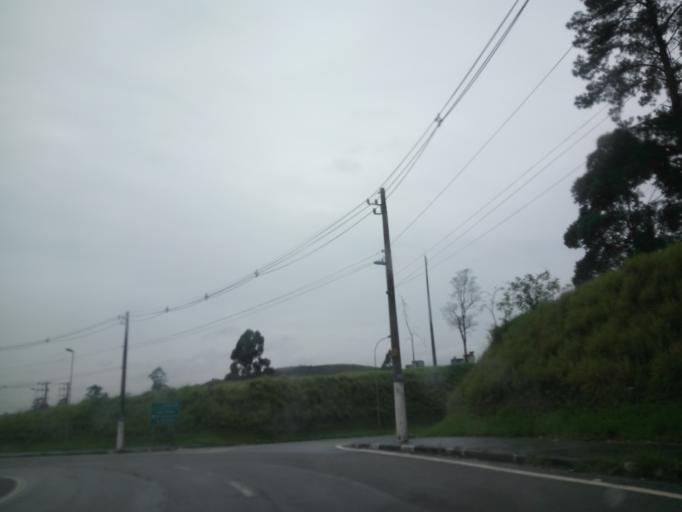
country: BR
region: Sao Paulo
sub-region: Sao Bernardo Do Campo
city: Sao Bernardo do Campo
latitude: -23.7590
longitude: -46.5943
